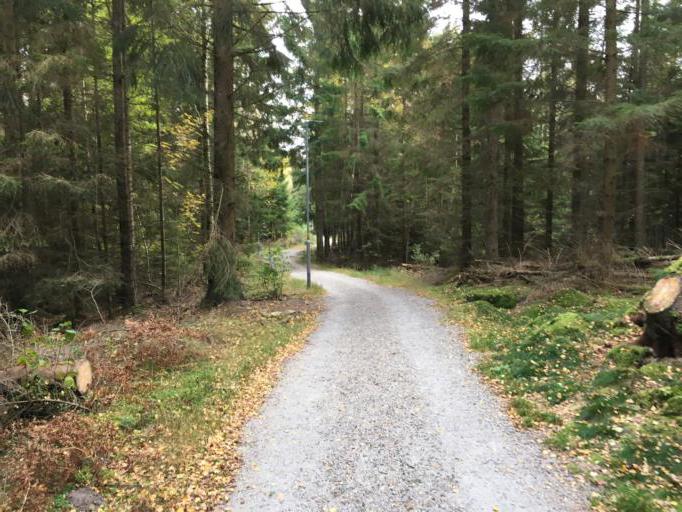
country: SE
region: Skane
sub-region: Hassleholms Kommun
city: Hassleholm
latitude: 56.1568
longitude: 13.7258
